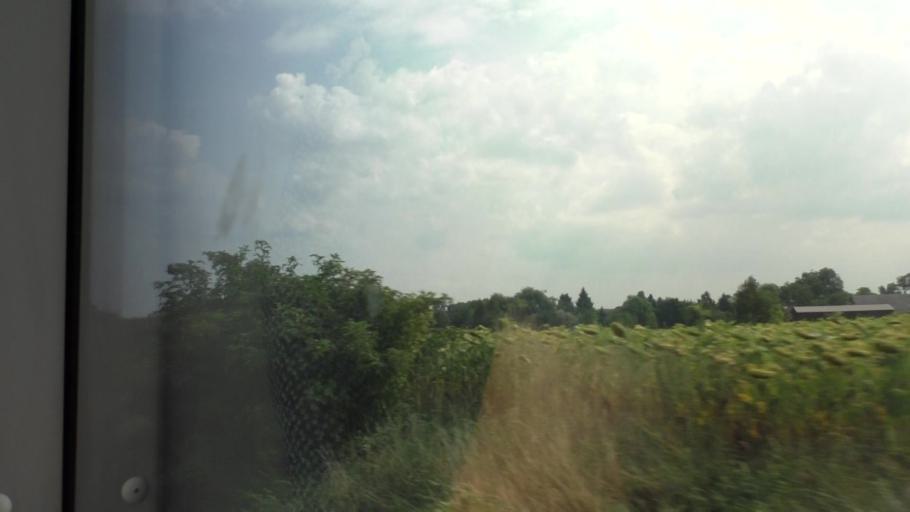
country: DE
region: Brandenburg
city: Tauche
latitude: 52.1753
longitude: 14.1978
